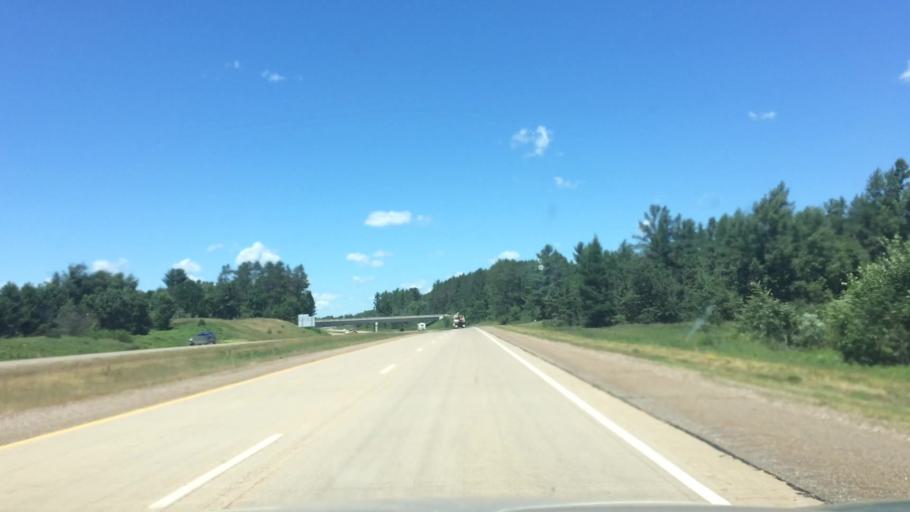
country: US
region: Wisconsin
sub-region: Lincoln County
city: Tomahawk
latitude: 45.4340
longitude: -89.6797
